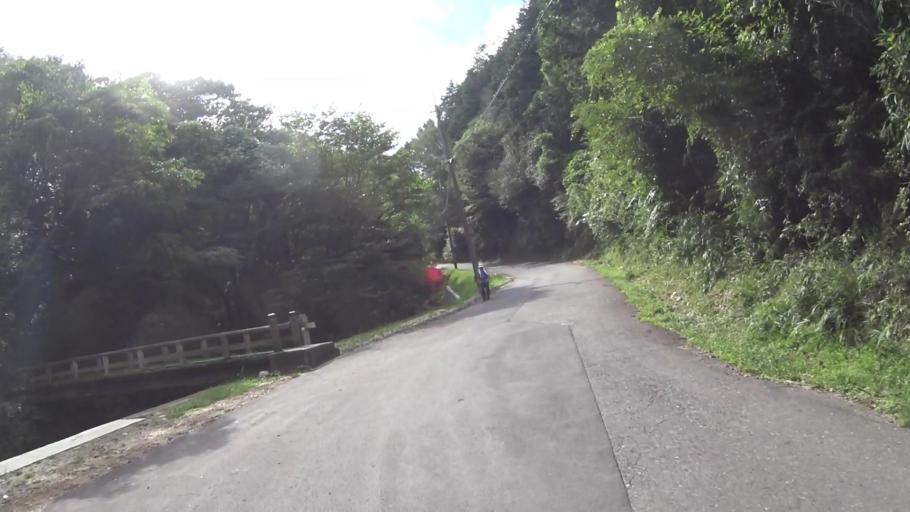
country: JP
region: Shiga Prefecture
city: Otsu-shi
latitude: 34.9481
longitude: 135.8790
